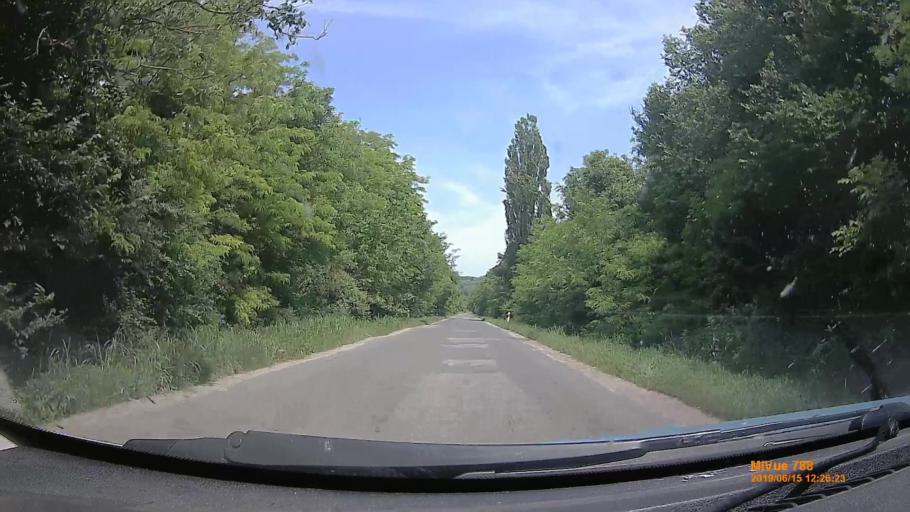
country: HU
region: Baranya
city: Buekkoesd
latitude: 46.1206
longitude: 17.9989
